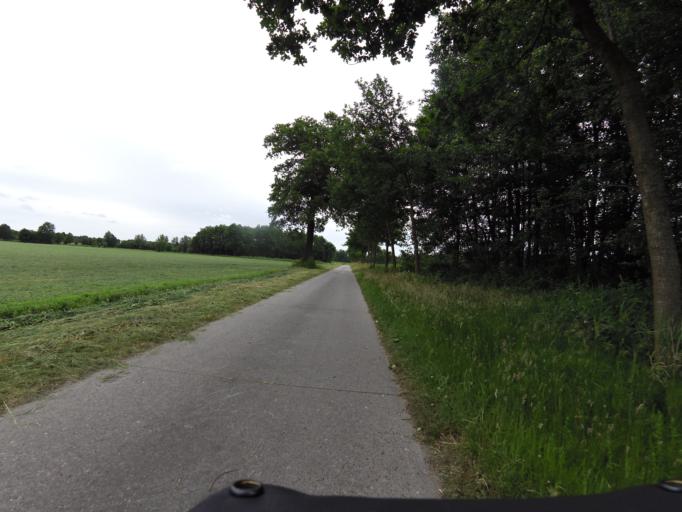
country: NL
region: North Brabant
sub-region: Gemeente Goirle
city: Goirle
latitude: 51.4447
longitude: 5.0553
